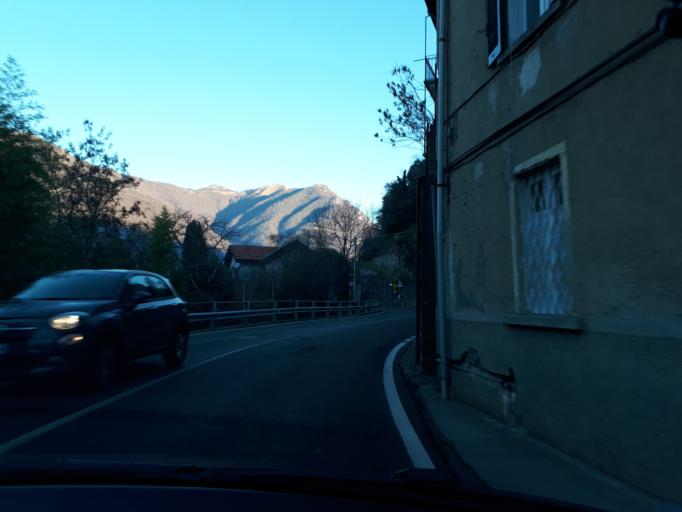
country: IT
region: Lombardy
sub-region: Provincia di Como
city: Blevio
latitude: 45.8462
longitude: 9.1064
